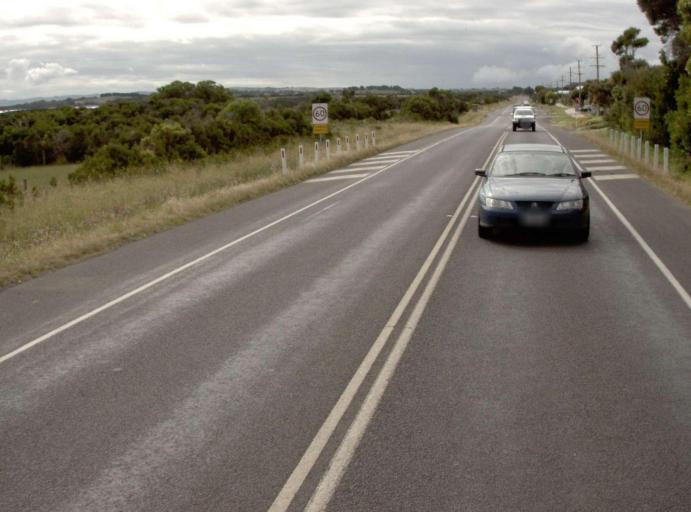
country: AU
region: Victoria
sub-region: Bass Coast
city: Phillip Island
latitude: -38.5068
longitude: 145.2894
